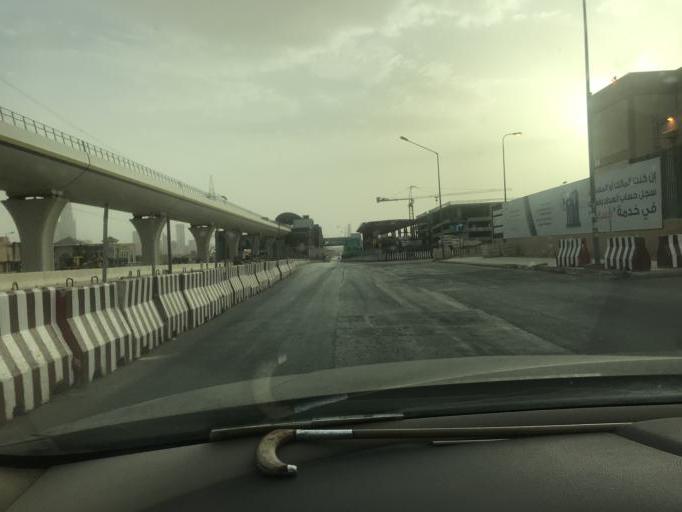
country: SA
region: Ar Riyad
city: Riyadh
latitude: 24.7879
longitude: 46.6632
